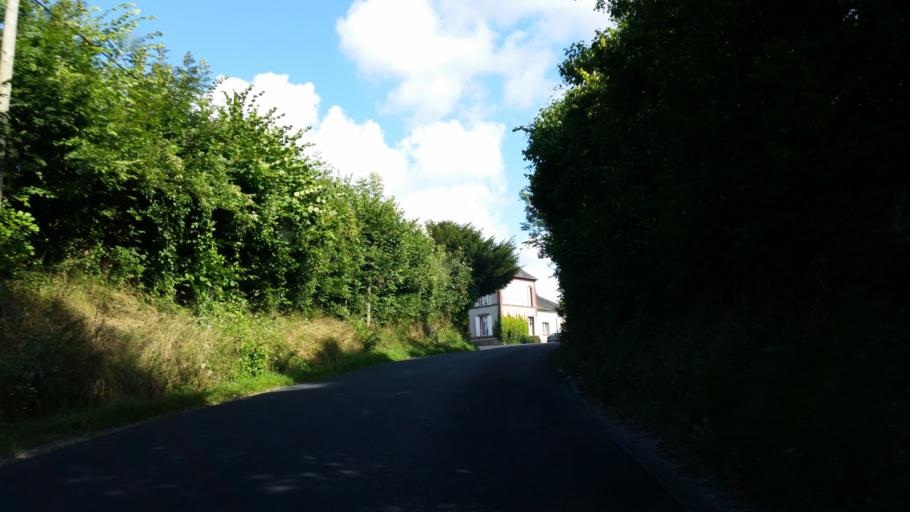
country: FR
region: Lower Normandy
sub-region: Departement du Calvados
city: Touques
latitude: 49.3382
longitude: 0.1177
